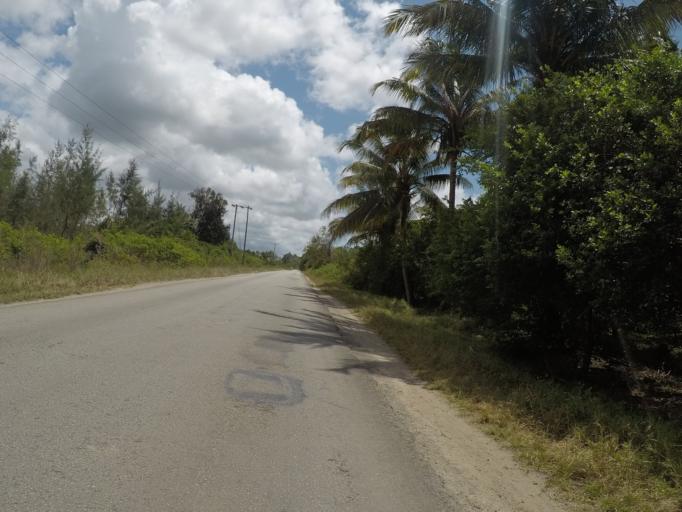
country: TZ
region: Zanzibar Central/South
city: Nganane
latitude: -6.2738
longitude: 39.4299
